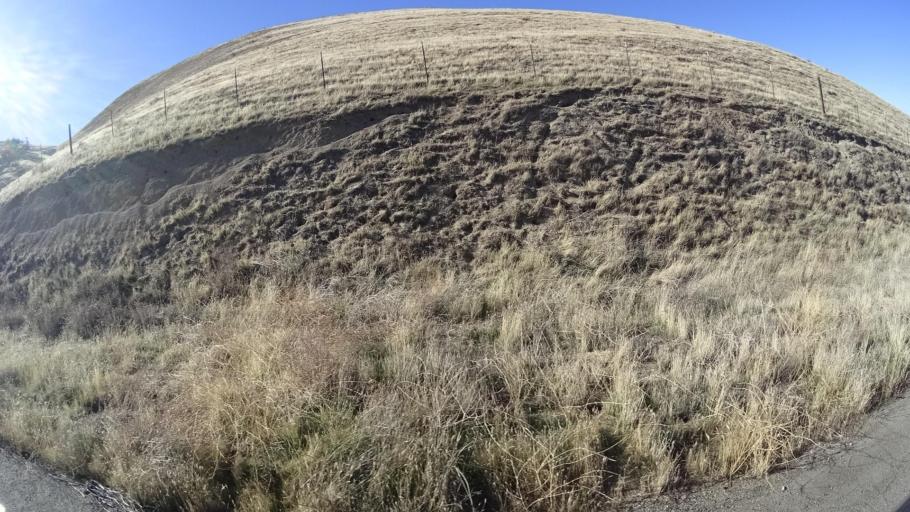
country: US
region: California
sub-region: Kern County
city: Maricopa
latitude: 34.9525
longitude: -119.4067
